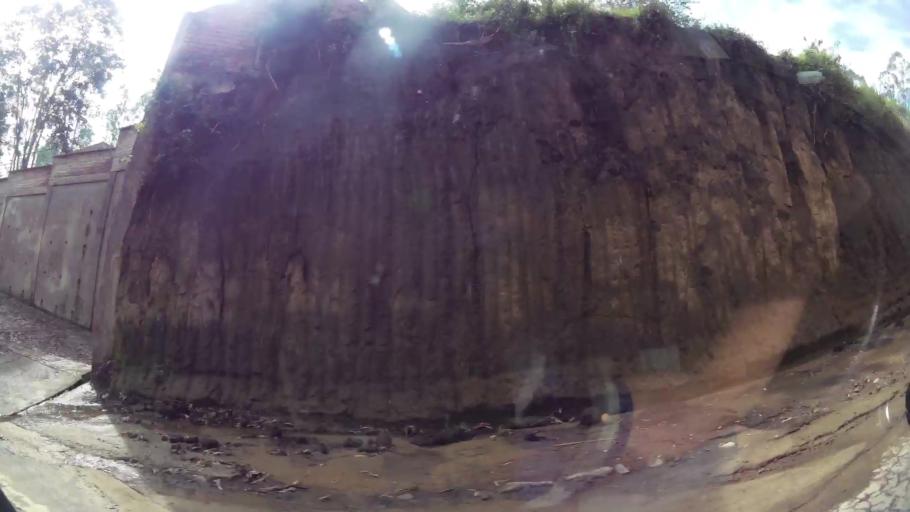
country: EC
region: Pichincha
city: Sangolqui
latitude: -0.3059
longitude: -78.4244
